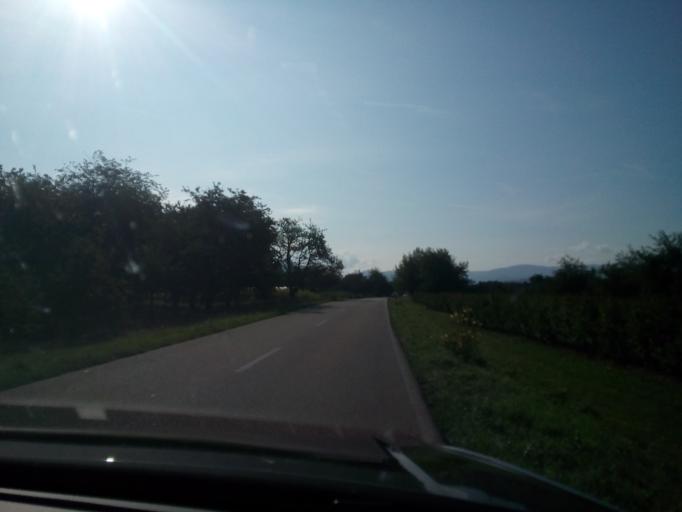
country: DE
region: Baden-Wuerttemberg
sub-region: Freiburg Region
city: Haslach
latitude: 48.5710
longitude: 8.0363
